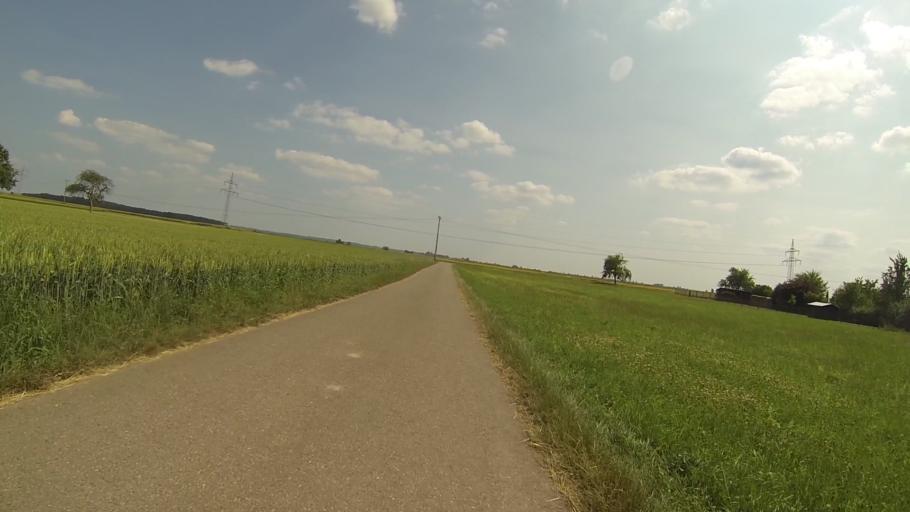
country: DE
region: Baden-Wuerttemberg
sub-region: Regierungsbezirk Stuttgart
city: Niederstotzingen
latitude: 48.5320
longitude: 10.2485
